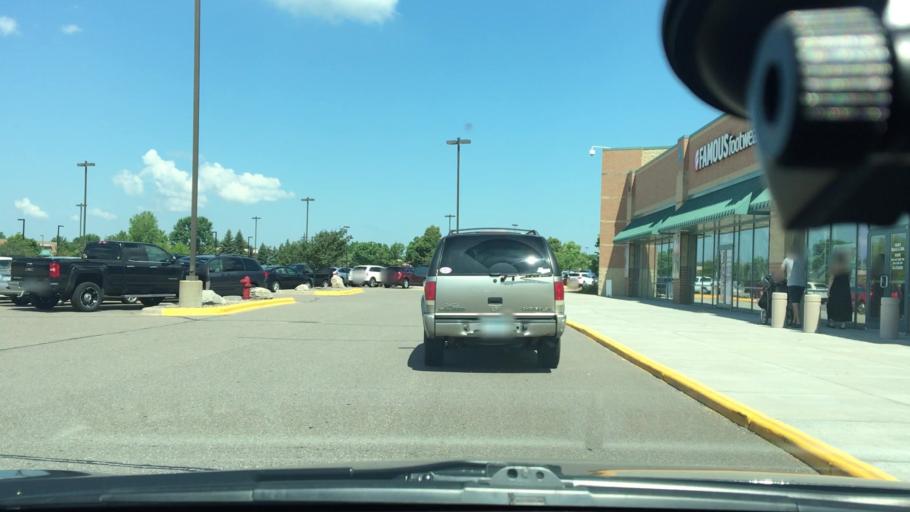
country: US
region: Minnesota
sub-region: Hennepin County
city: Maple Grove
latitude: 45.1005
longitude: -93.4480
